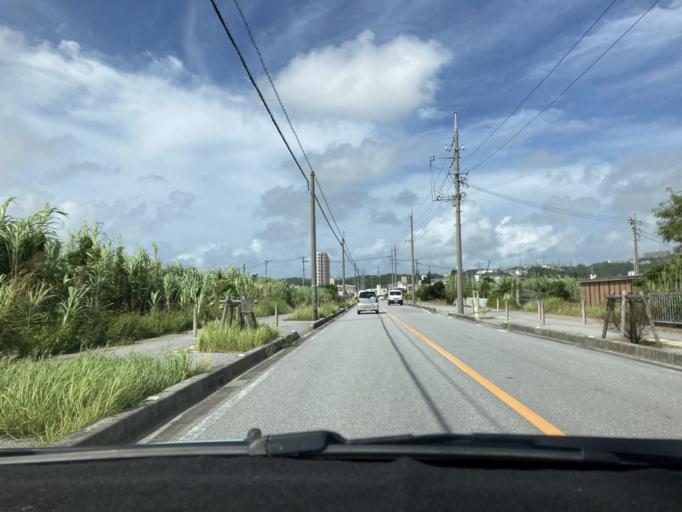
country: JP
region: Okinawa
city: Ginowan
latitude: 26.2226
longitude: 127.7714
